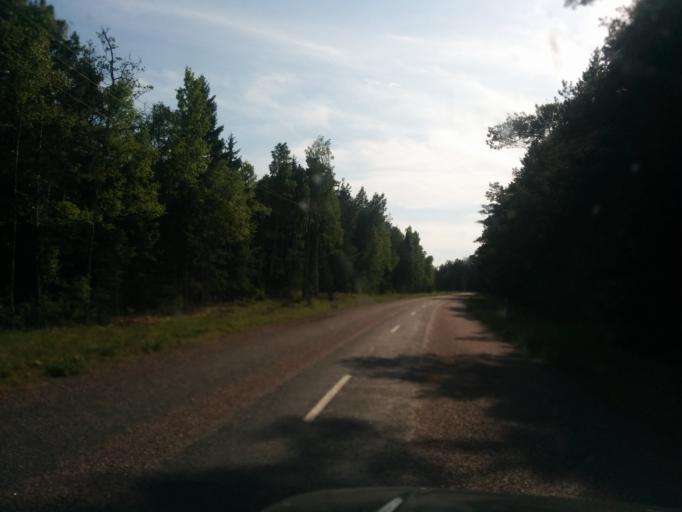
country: LV
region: Dundaga
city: Dundaga
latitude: 57.6675
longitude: 22.3105
